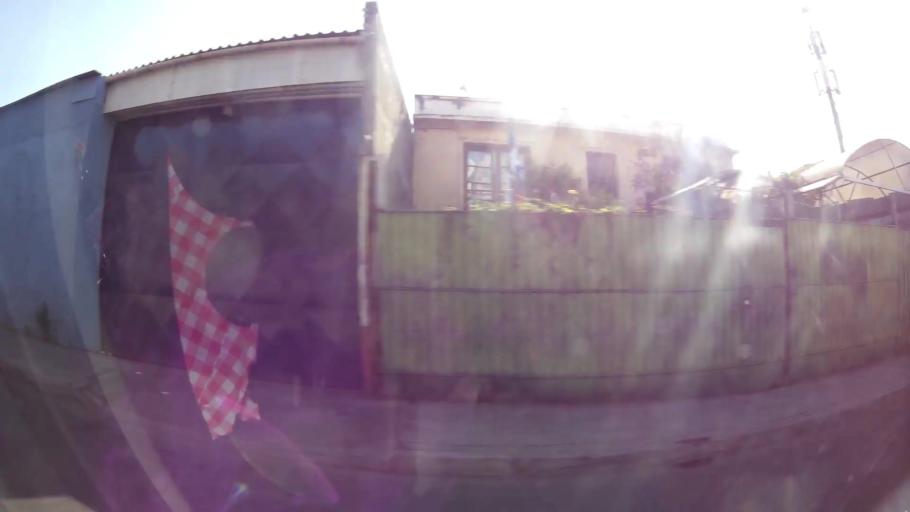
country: CL
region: Santiago Metropolitan
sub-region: Provincia de Santiago
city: Santiago
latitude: -33.4287
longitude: -70.6768
